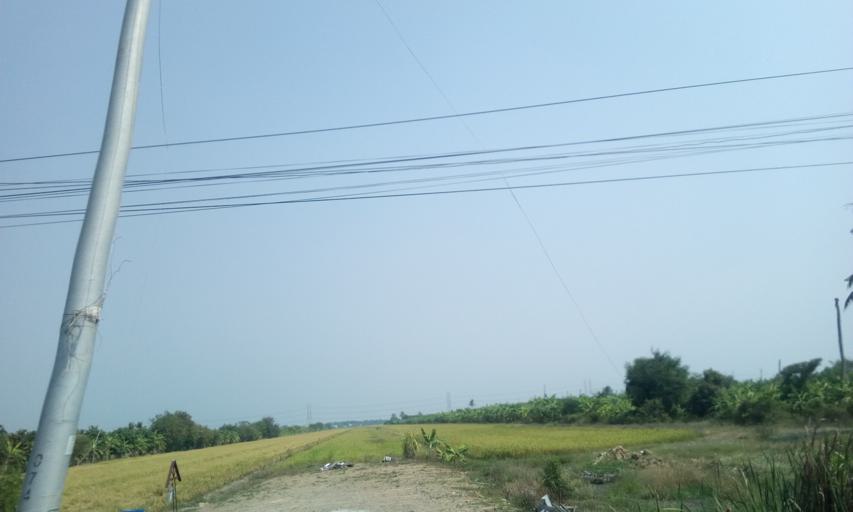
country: TH
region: Pathum Thani
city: Ban Lam Luk Ka
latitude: 13.9956
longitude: 100.7566
